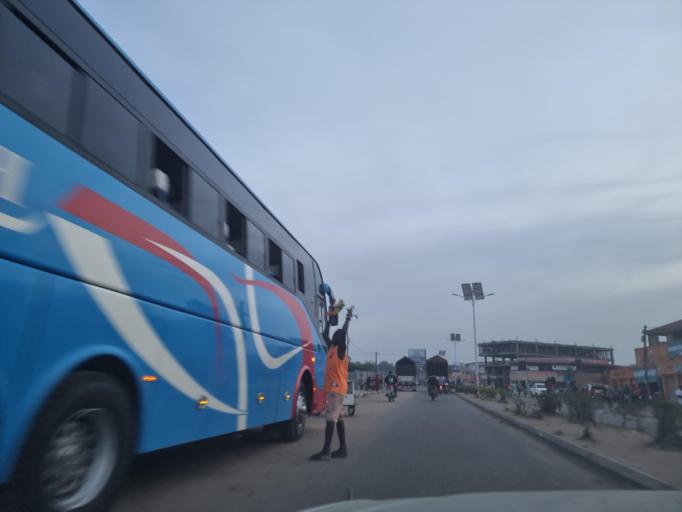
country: UG
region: Northern Region
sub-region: Arua District
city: Arua
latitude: 3.0234
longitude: 30.9126
